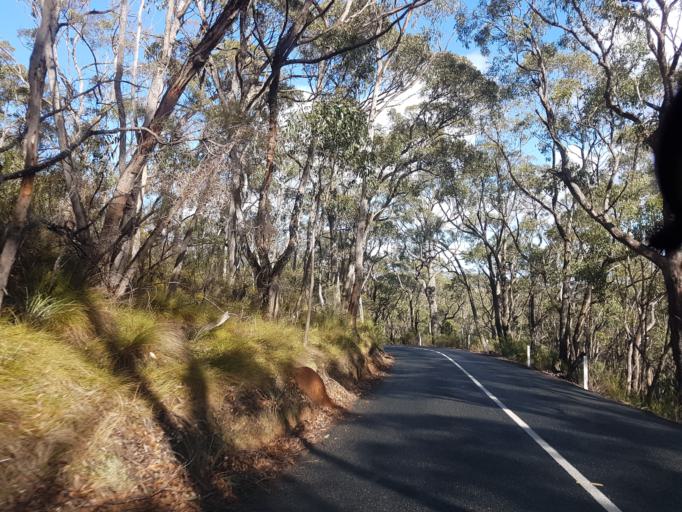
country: AU
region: South Australia
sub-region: Adelaide Hills
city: Heathfield
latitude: -35.0337
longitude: 138.7127
